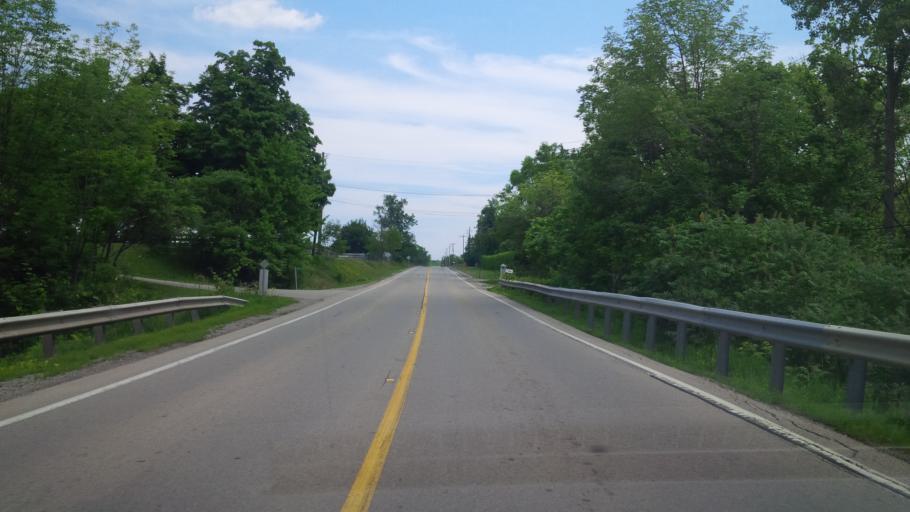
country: CA
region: Ontario
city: Burlington
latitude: 43.4411
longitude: -79.8679
